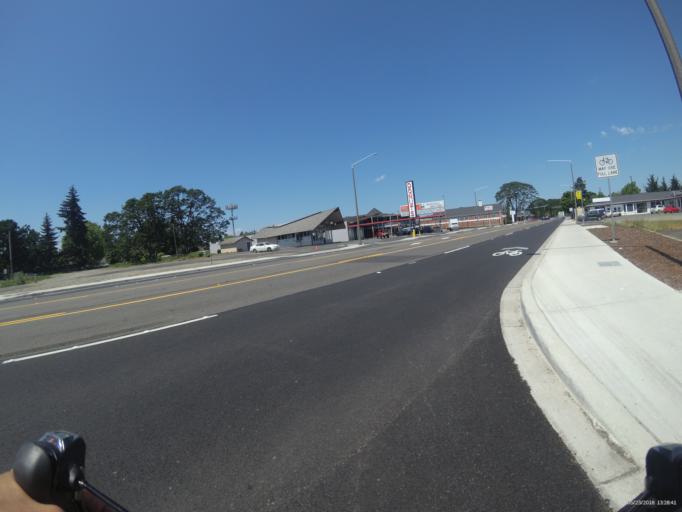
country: US
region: Washington
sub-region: Pierce County
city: Lakewood
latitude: 47.1684
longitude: -122.5193
